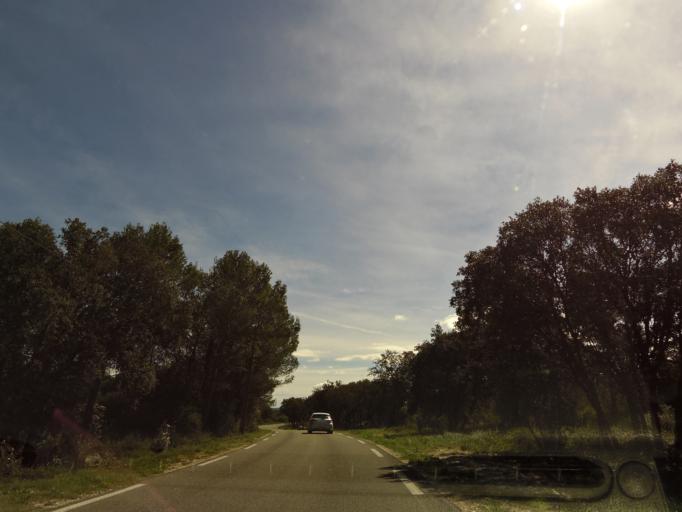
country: FR
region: Languedoc-Roussillon
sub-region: Departement du Gard
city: Langlade
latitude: 43.7910
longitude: 4.2608
